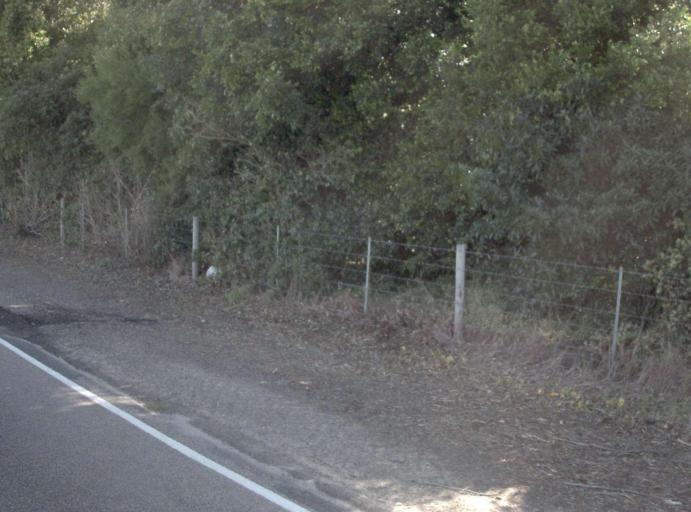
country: AU
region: Victoria
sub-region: East Gippsland
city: Lakes Entrance
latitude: -37.7358
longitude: 148.5048
